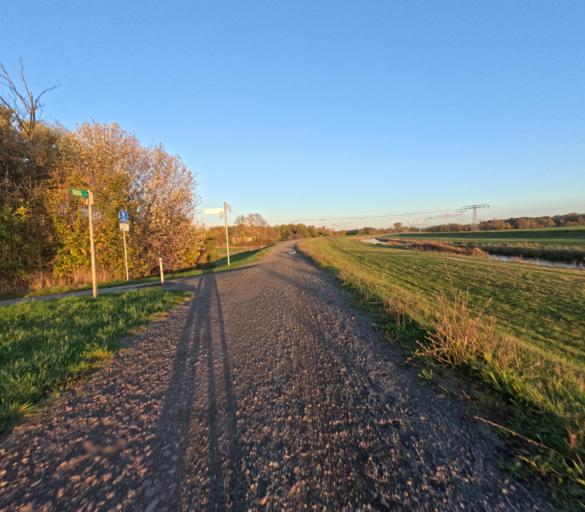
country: DE
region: Saxony
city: Schkeuditz
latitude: 51.3819
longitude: 12.2584
